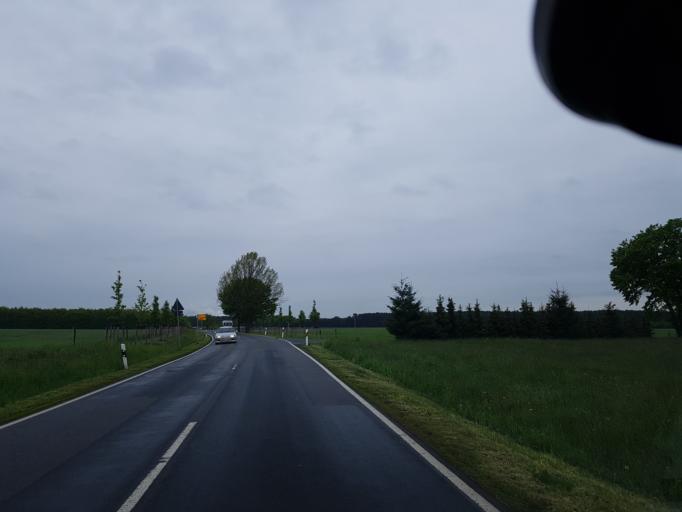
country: DE
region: Saxony
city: Gross Duben
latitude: 51.6326
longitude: 14.5159
